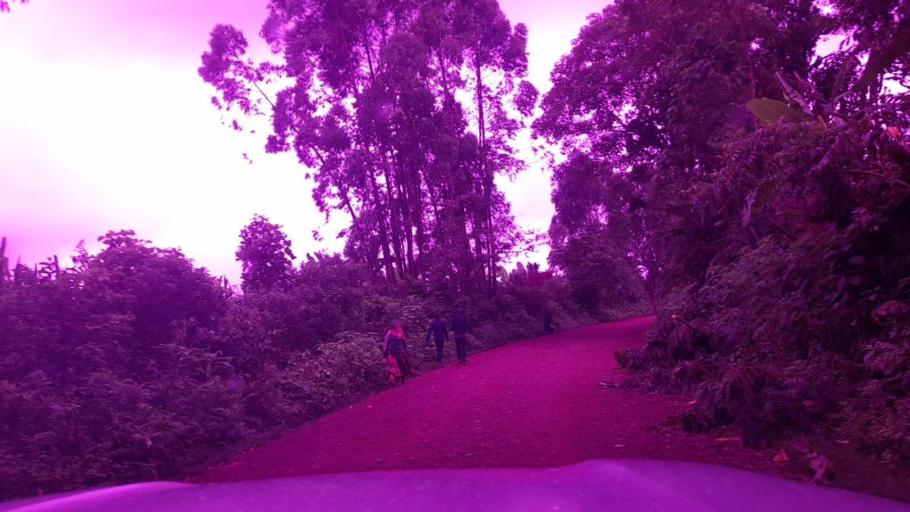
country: ET
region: Southern Nations, Nationalities, and People's Region
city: Bonga
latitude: 7.5850
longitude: 36.0163
